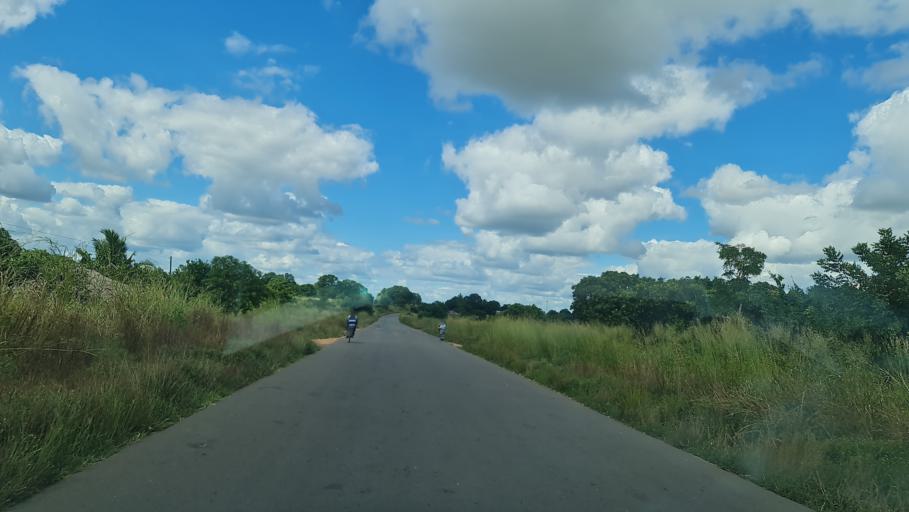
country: MZ
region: Zambezia
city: Quelimane
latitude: -17.5126
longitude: 36.2568
